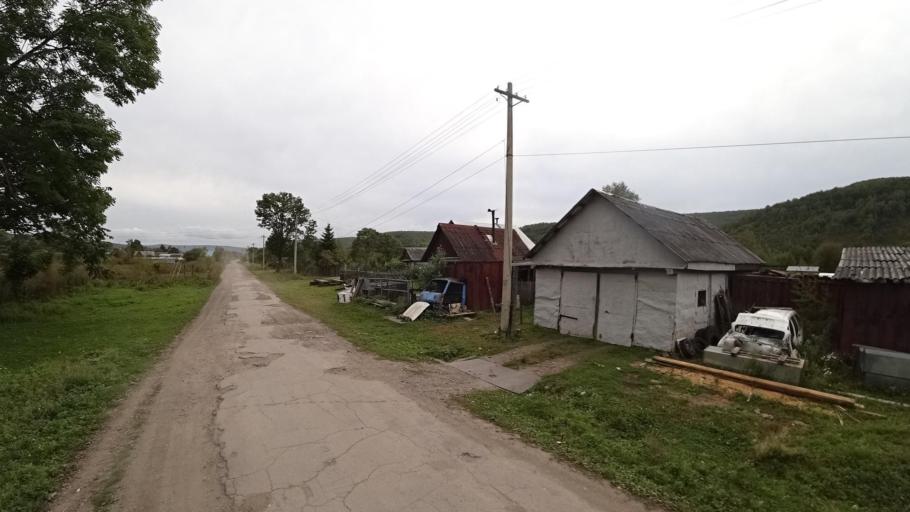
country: RU
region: Jewish Autonomous Oblast
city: Khingansk
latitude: 49.0383
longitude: 131.0496
